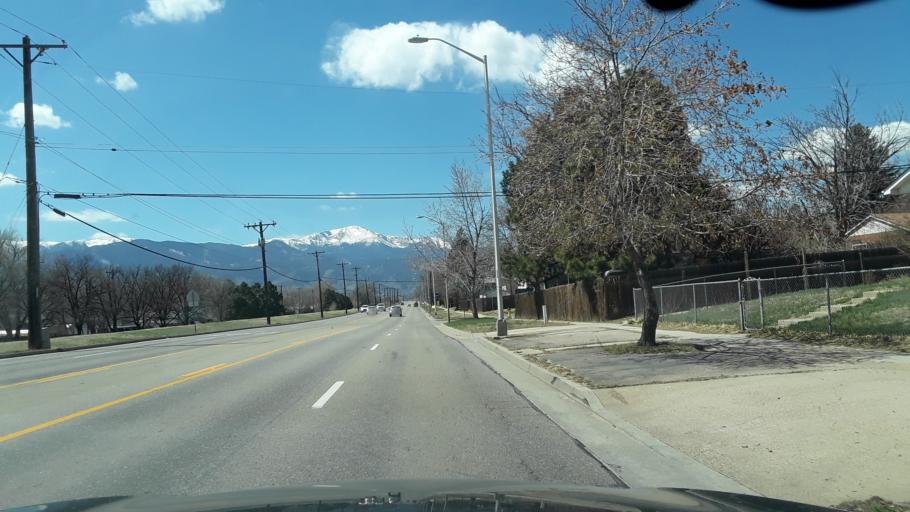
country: US
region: Colorado
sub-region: El Paso County
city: Colorado Springs
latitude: 38.8594
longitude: -104.7661
